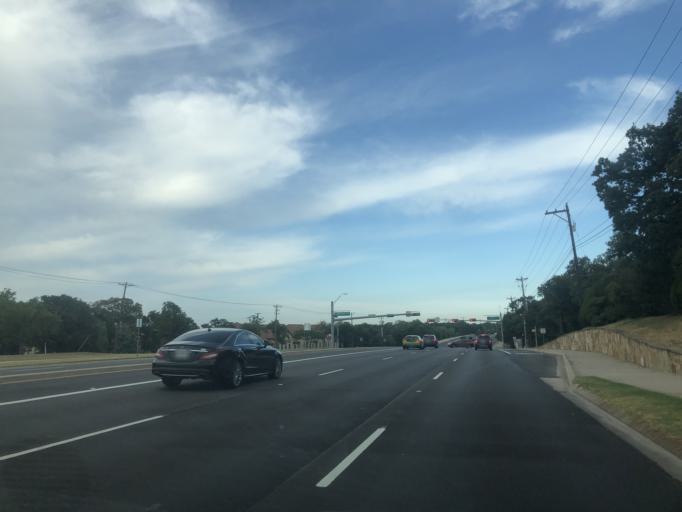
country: US
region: Texas
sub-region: Tarrant County
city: Keller
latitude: 32.9349
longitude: -97.1942
